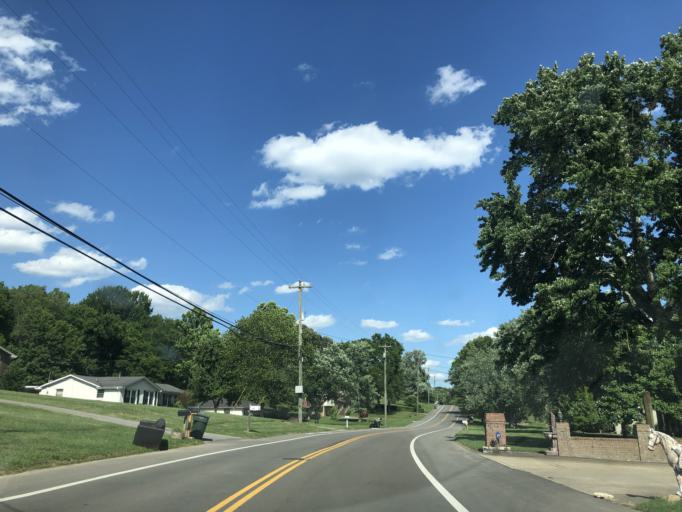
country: US
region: Tennessee
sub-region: Davidson County
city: Belle Meade
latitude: 36.0613
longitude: -86.9323
